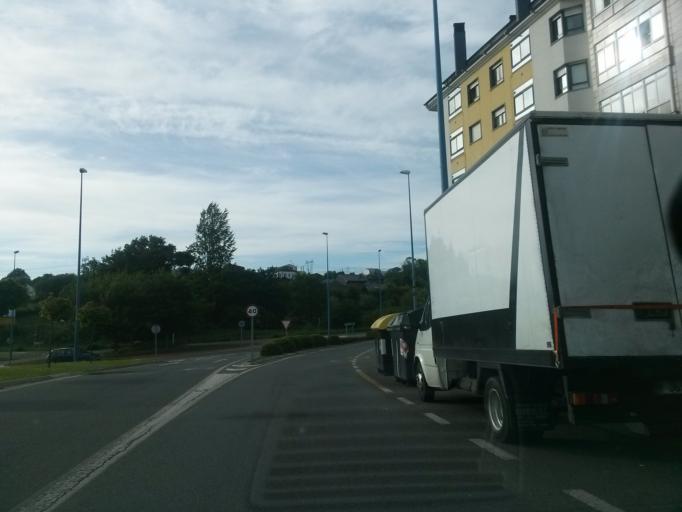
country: ES
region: Galicia
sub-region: Provincia de Lugo
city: Lugo
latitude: 43.0102
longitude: -7.5742
